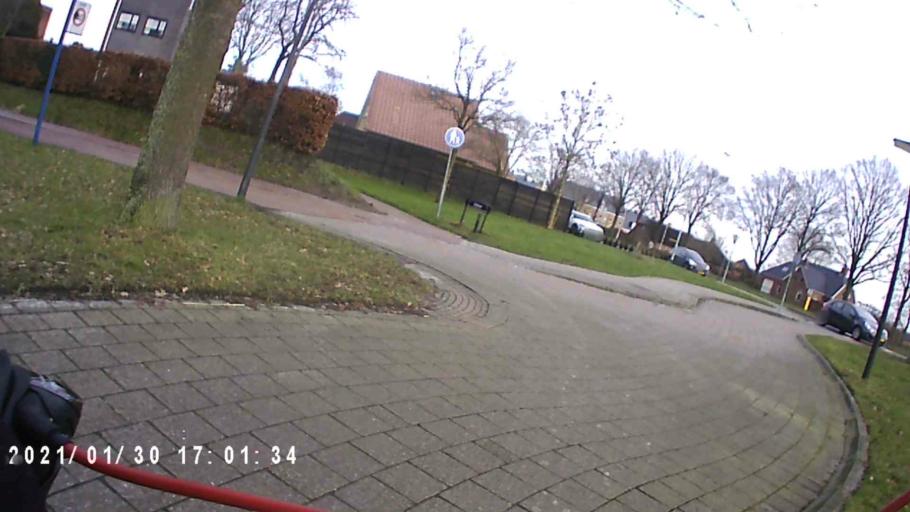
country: NL
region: Groningen
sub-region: Gemeente Leek
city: Leek
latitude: 53.1511
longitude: 6.3716
